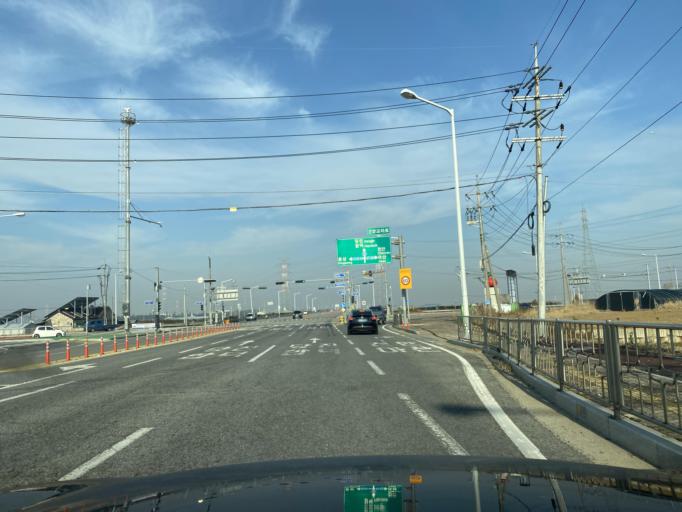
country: KR
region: Chungcheongnam-do
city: Yesan
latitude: 36.7385
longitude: 126.8594
